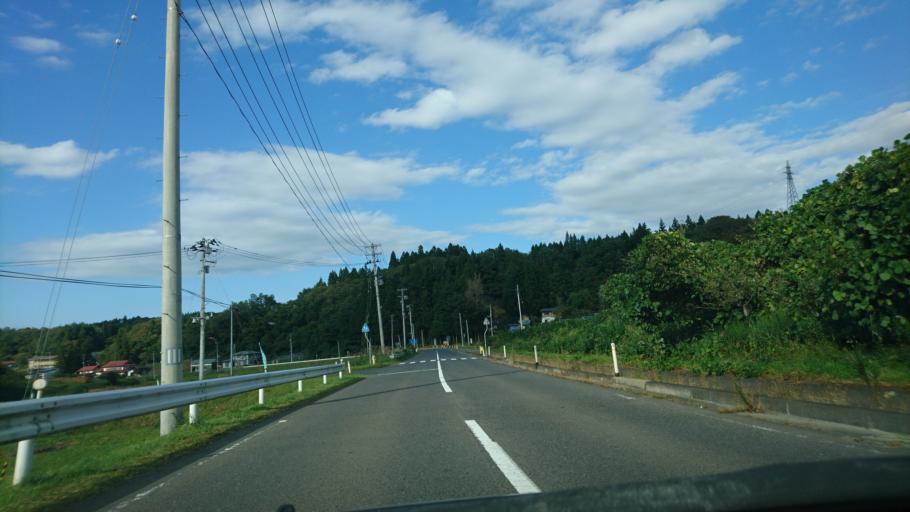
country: JP
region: Iwate
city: Ichinoseki
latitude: 38.8902
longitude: 141.3318
